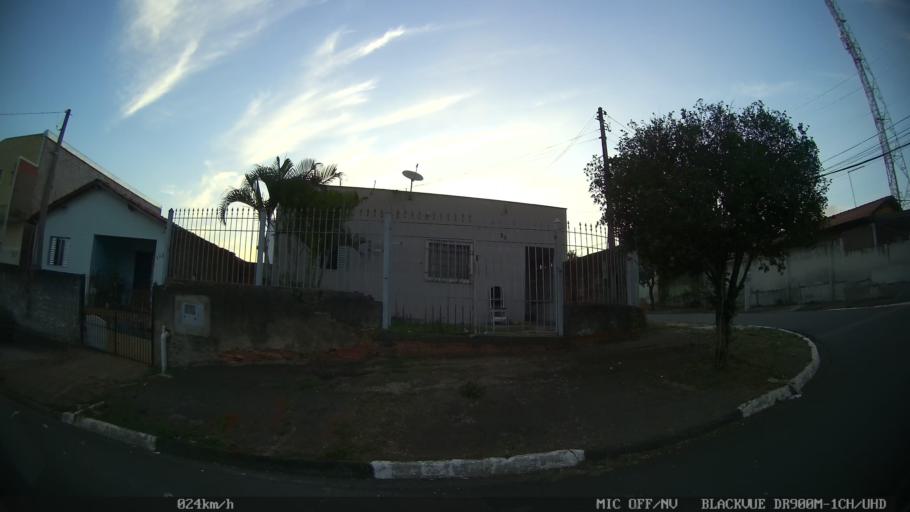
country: BR
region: Sao Paulo
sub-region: Hortolandia
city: Hortolandia
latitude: -22.8591
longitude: -47.2145
